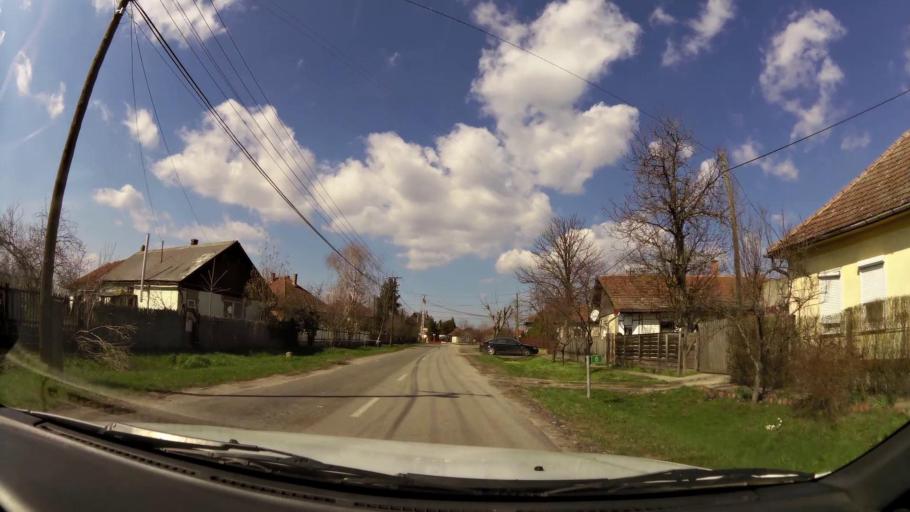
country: HU
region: Pest
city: Tapiogyorgye
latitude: 47.3290
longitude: 19.9456
